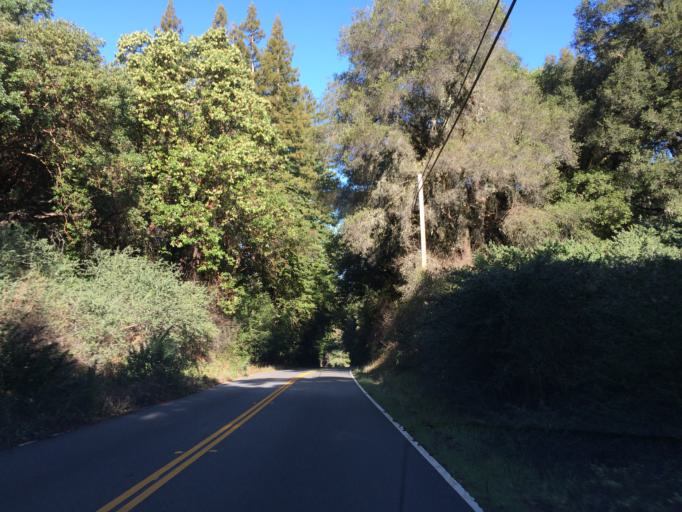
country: US
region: California
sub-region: Santa Cruz County
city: Boulder Creek
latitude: 37.1333
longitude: -122.1695
